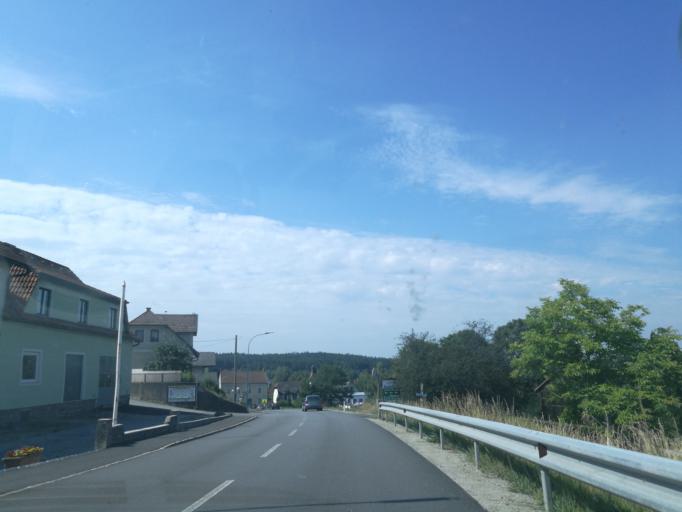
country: AT
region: Lower Austria
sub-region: Politischer Bezirk Gmund
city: Heidenreichstein
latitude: 48.8641
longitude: 15.1264
